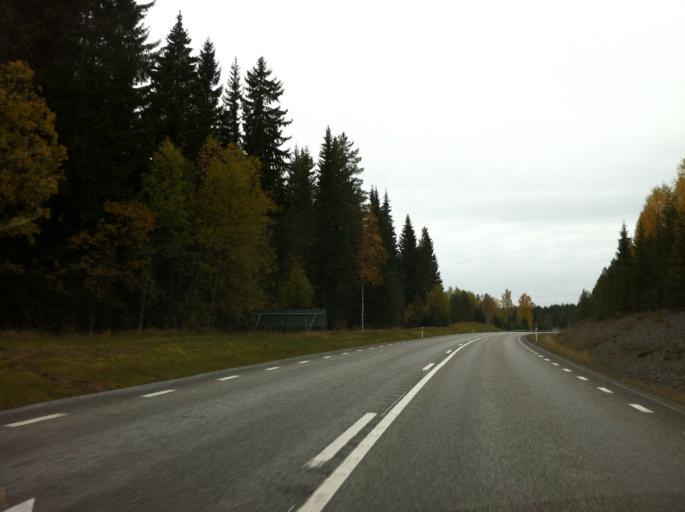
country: SE
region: OErebro
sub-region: Ljusnarsbergs Kommun
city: Kopparberg
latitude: 59.8692
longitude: 15.0505
